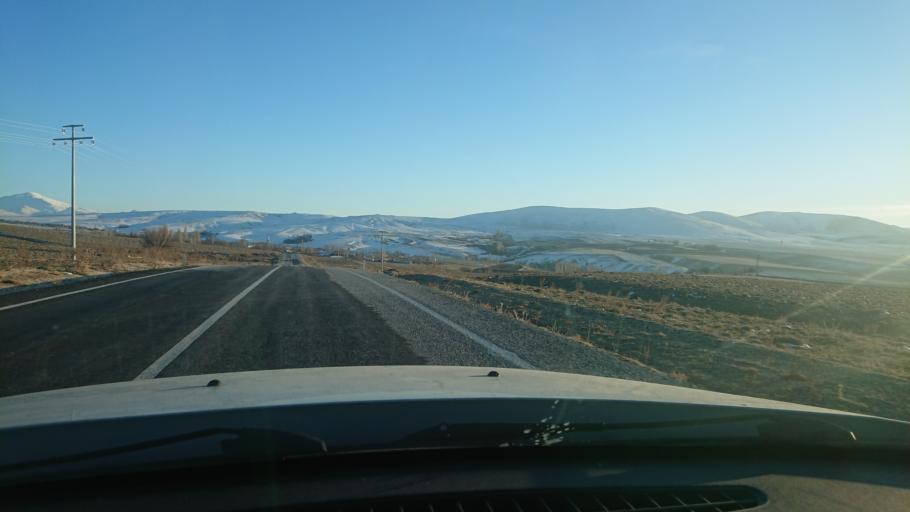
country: TR
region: Aksaray
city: Ortakoy
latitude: 38.7638
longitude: 33.9319
